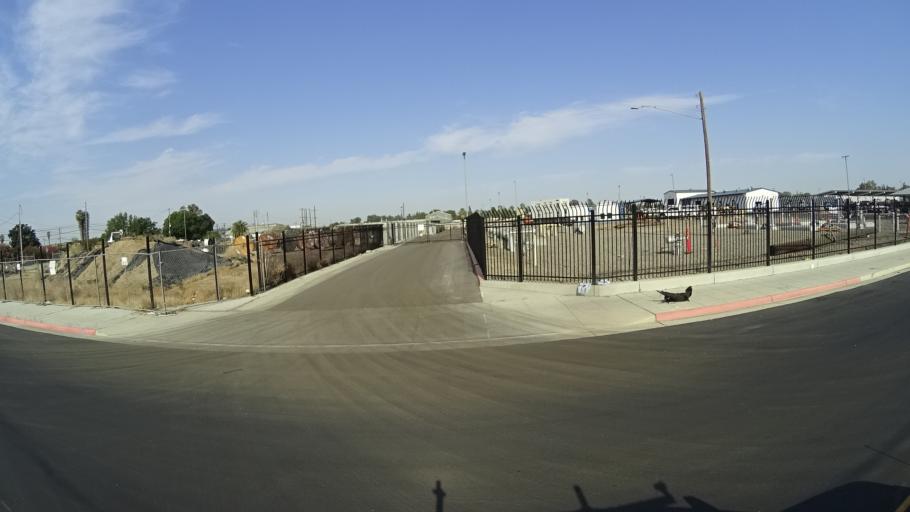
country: US
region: California
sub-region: Fresno County
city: Fresno
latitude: 36.7447
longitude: -119.8130
